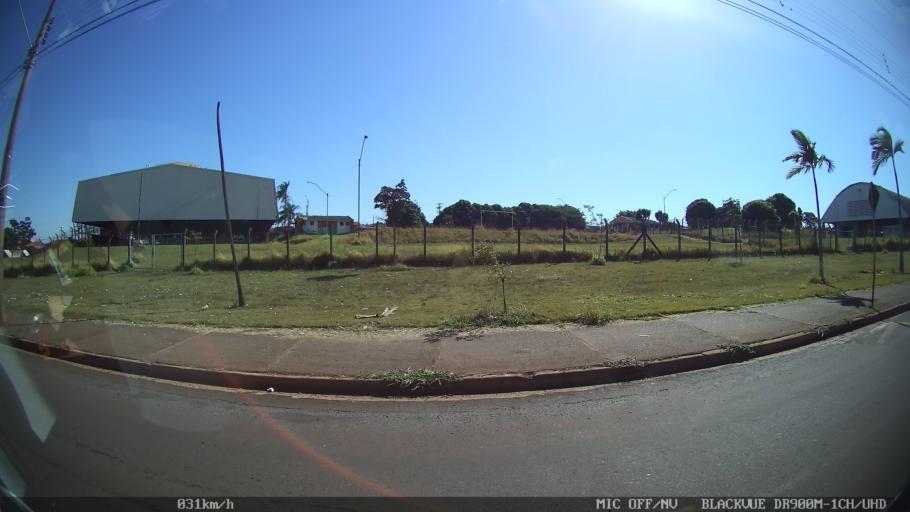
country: BR
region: Sao Paulo
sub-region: Batatais
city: Batatais
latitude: -20.8867
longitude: -47.5740
